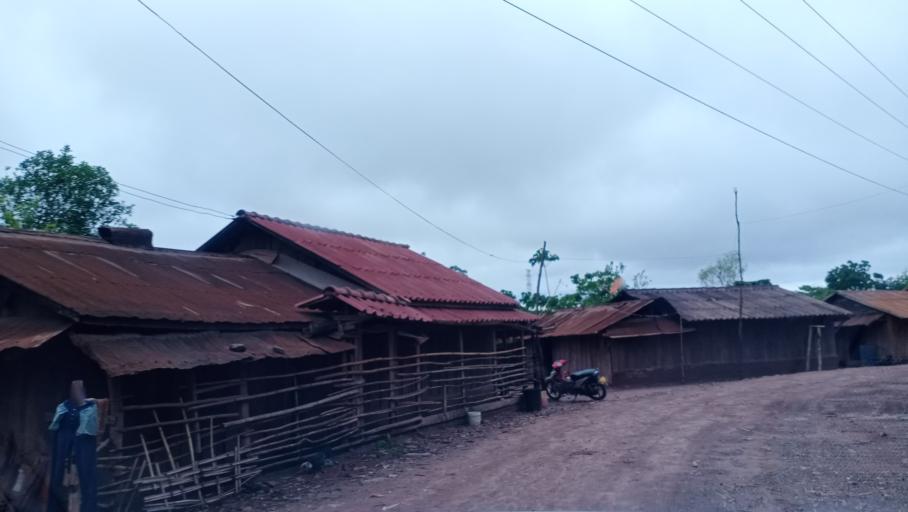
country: LA
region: Phongsali
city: Phongsali
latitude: 21.3387
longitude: 102.0823
